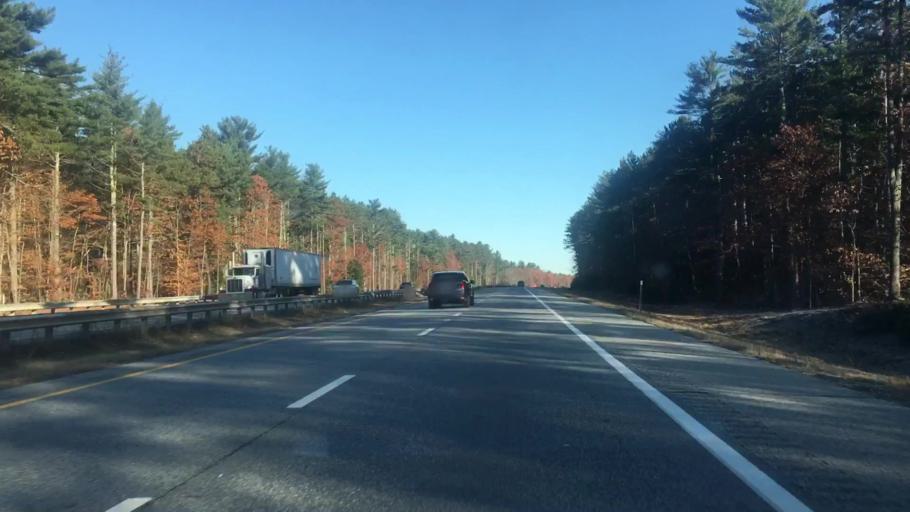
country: US
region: Maine
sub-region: Cumberland County
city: New Gloucester
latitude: 43.9927
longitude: -70.3092
